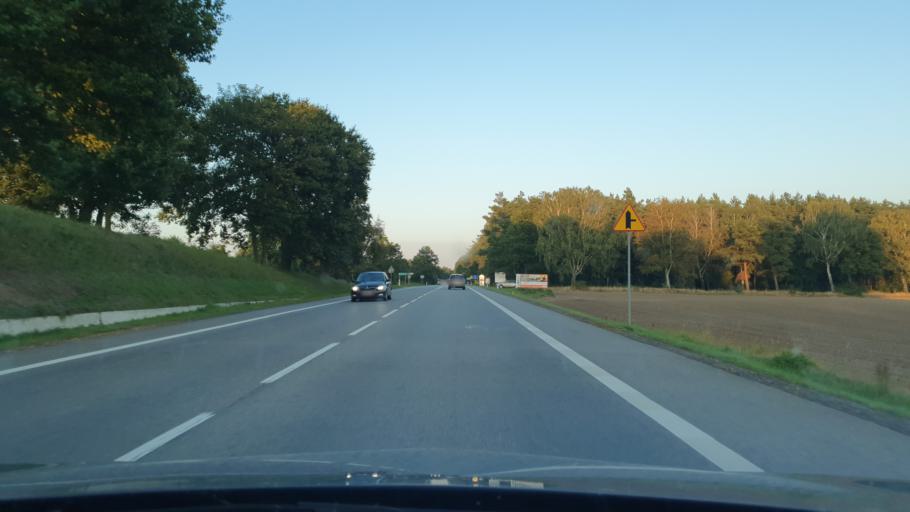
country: PL
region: Pomeranian Voivodeship
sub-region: Powiat slupski
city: Potegowo
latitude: 54.4806
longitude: 17.5483
